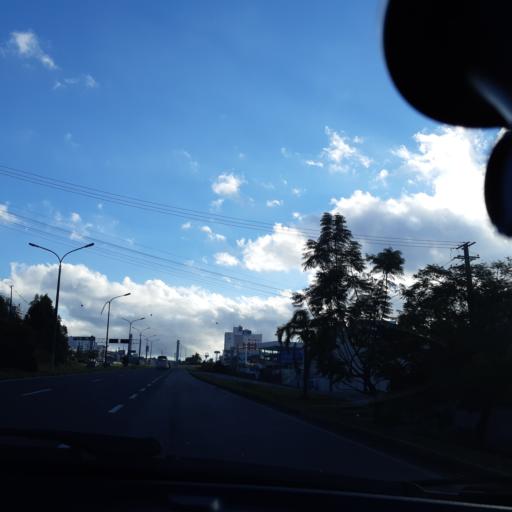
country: BR
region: Rio Grande do Sul
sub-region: Caxias Do Sul
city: Caxias do Sul
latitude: -29.1751
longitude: -51.2104
